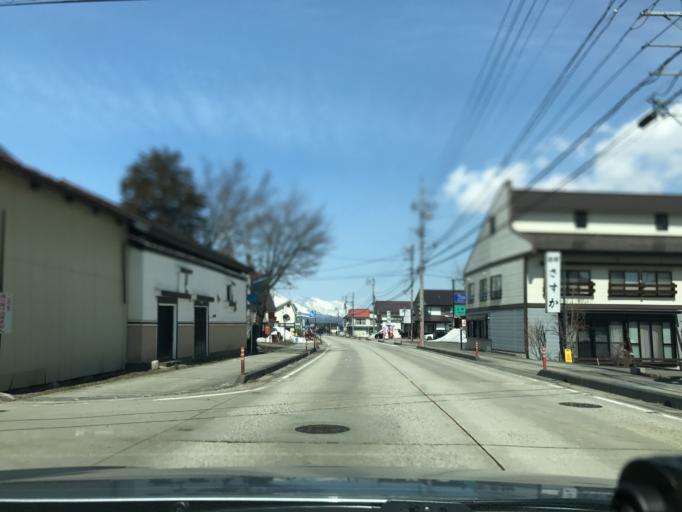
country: JP
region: Nagano
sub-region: Kitaazumi Gun
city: Hakuba
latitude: 36.6588
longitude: 137.8483
